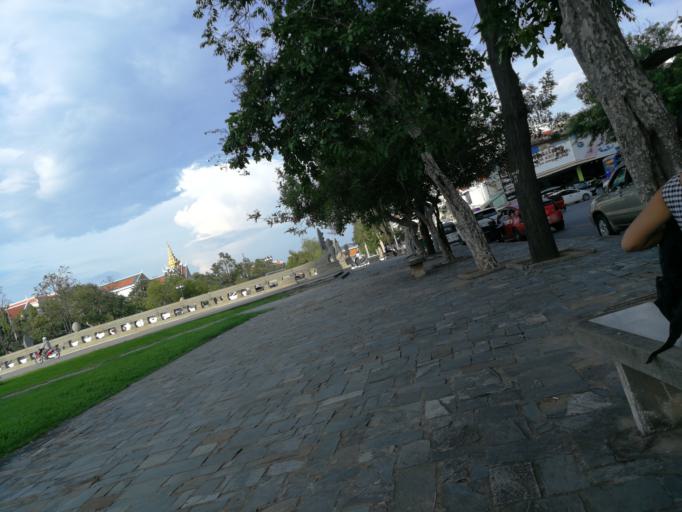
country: KH
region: Phnom Penh
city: Phnom Penh
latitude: 11.5732
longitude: 104.9230
